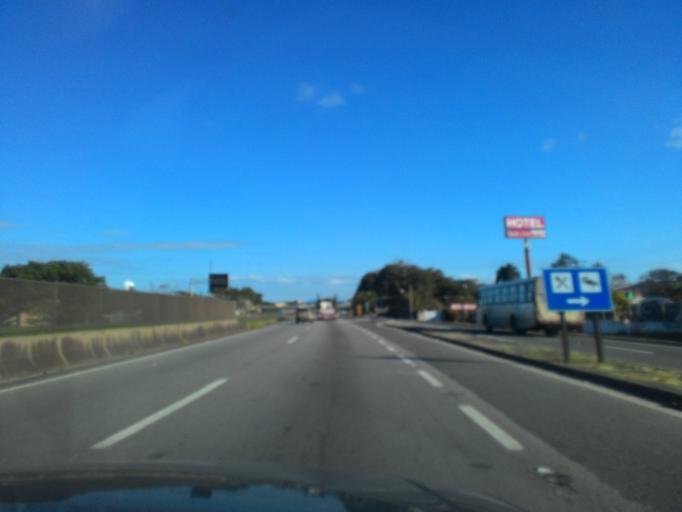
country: BR
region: Sao Paulo
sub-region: Registro
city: Registro
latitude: -24.5032
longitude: -47.8476
